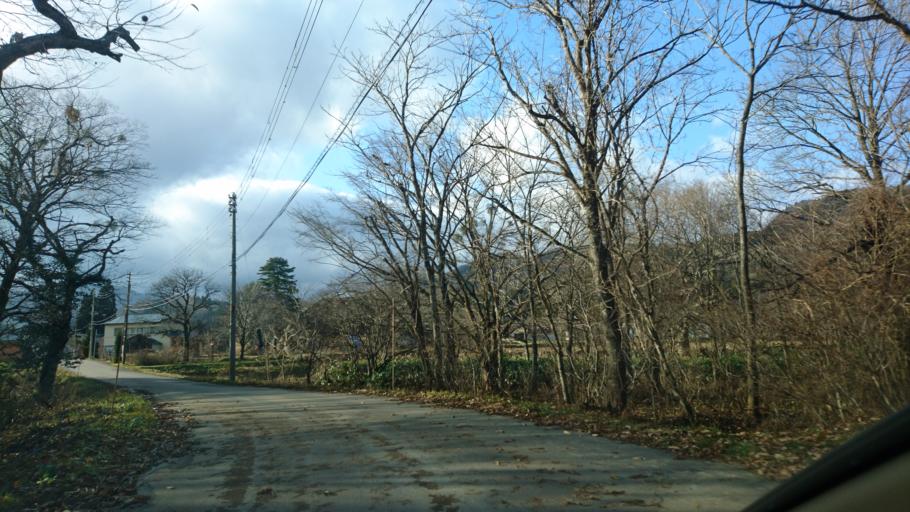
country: JP
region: Akita
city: Kakunodatemachi
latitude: 39.4821
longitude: 140.8062
